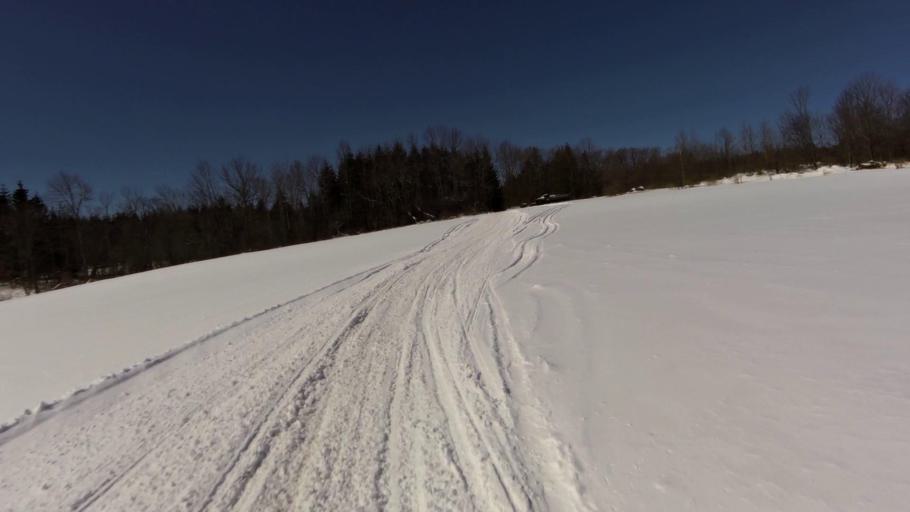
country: US
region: New York
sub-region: Allegany County
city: Houghton
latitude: 42.4087
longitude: -78.2853
